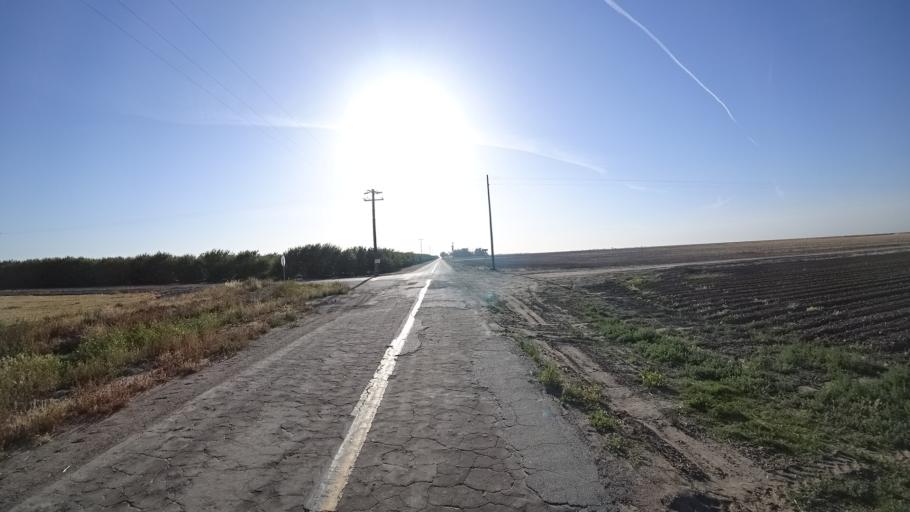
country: US
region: California
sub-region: Kings County
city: Stratford
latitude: 36.1600
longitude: -119.7806
